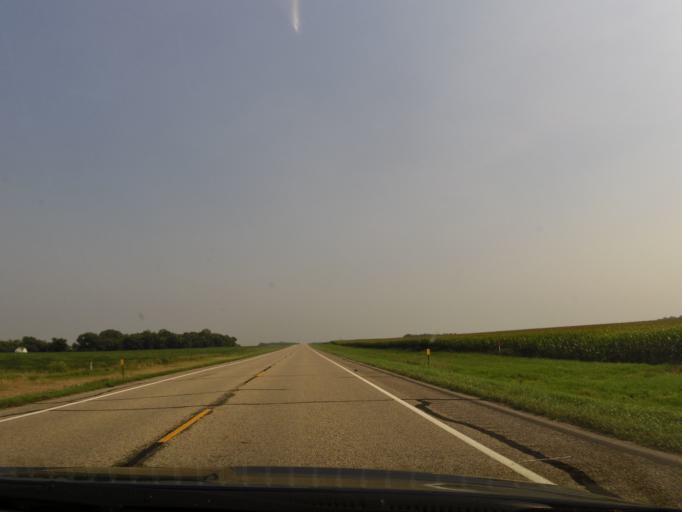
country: US
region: Minnesota
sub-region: Traverse County
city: Wheaton
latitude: 45.8636
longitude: -96.6973
